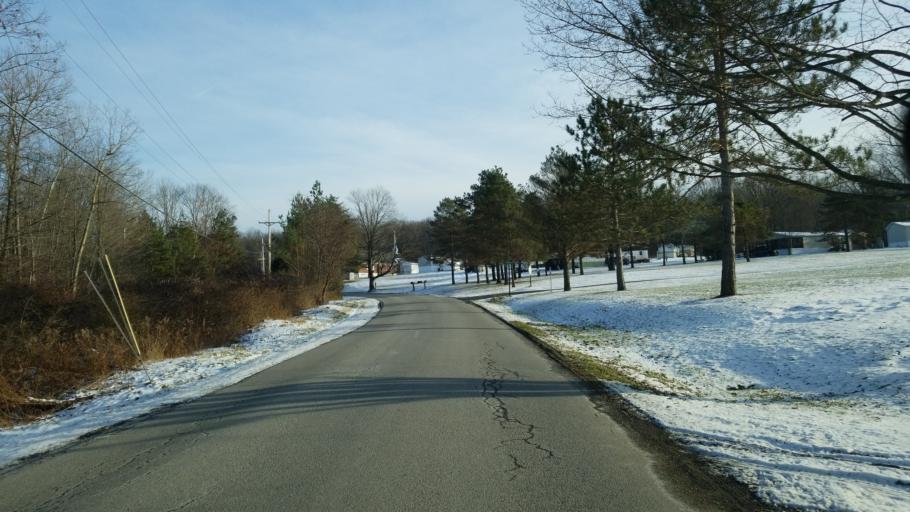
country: US
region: Pennsylvania
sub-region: Clearfield County
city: DuBois
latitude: 41.1104
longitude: -78.6992
